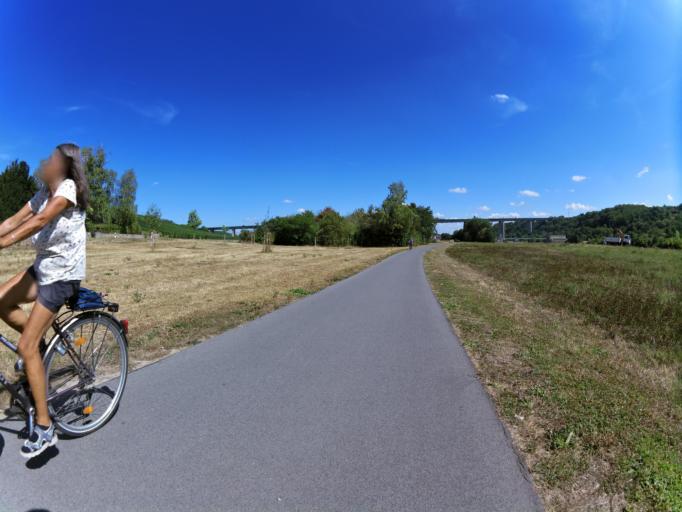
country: DE
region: Bavaria
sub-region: Regierungsbezirk Unterfranken
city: Frickenhausen
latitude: 49.6692
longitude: 10.1171
